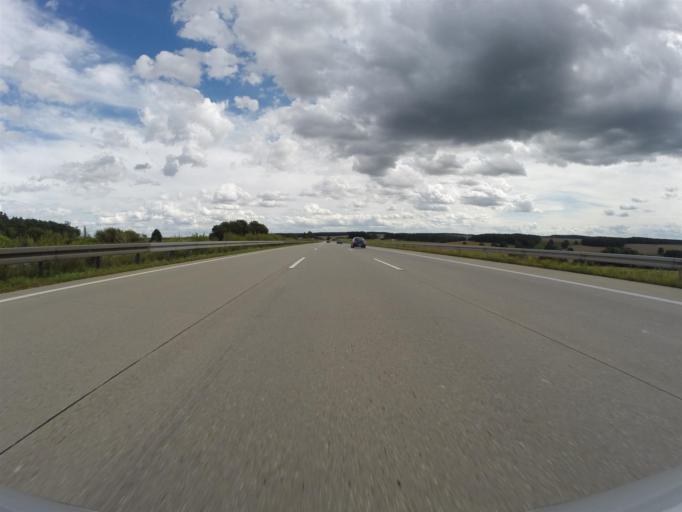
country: DE
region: Thuringia
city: Eineborn
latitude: 50.8351
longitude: 11.8730
